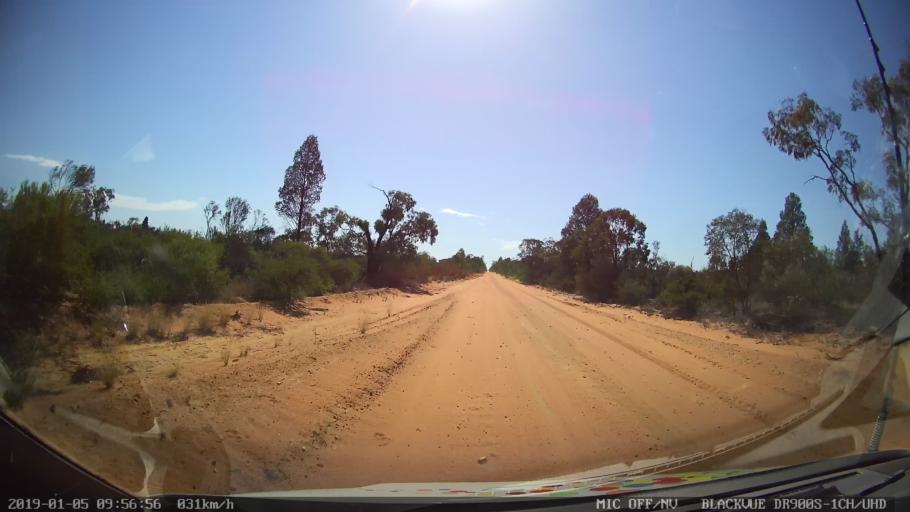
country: AU
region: New South Wales
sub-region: Gilgandra
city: Gilgandra
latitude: -31.6652
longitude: 148.7977
